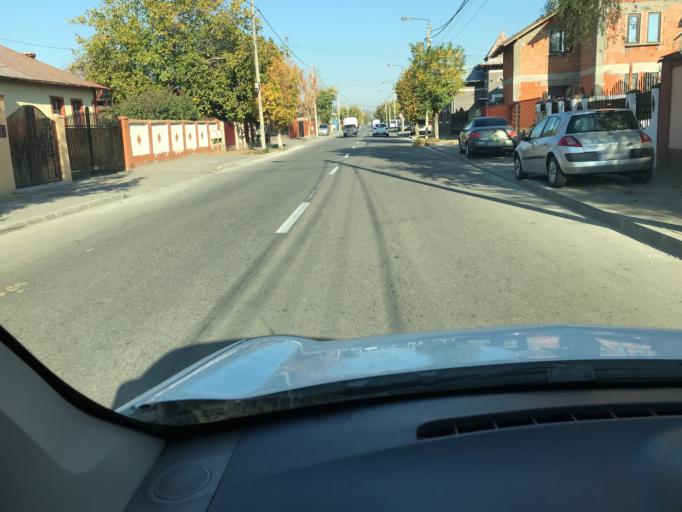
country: RO
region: Olt
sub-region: Municipiul Slatina
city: Slatina
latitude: 44.4347
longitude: 24.3504
